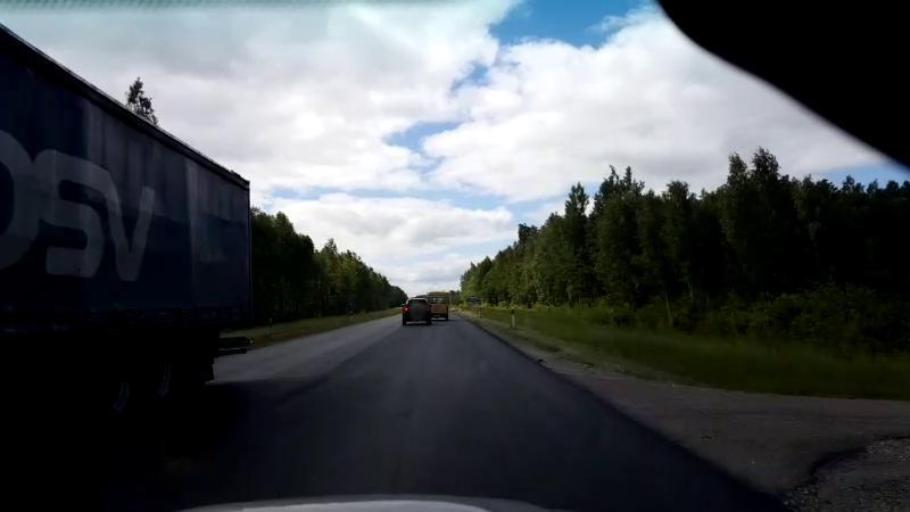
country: LV
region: Salacgrivas
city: Ainazi
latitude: 57.9706
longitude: 24.4507
